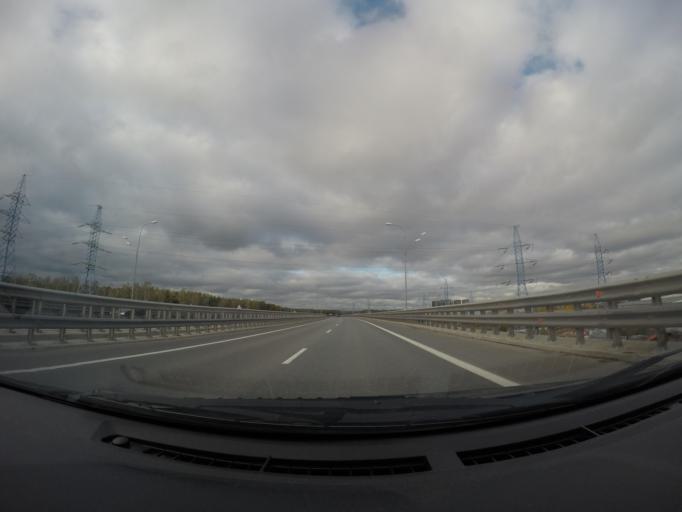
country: RU
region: Moskovskaya
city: Lesnoy Gorodok
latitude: 55.6644
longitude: 37.2247
